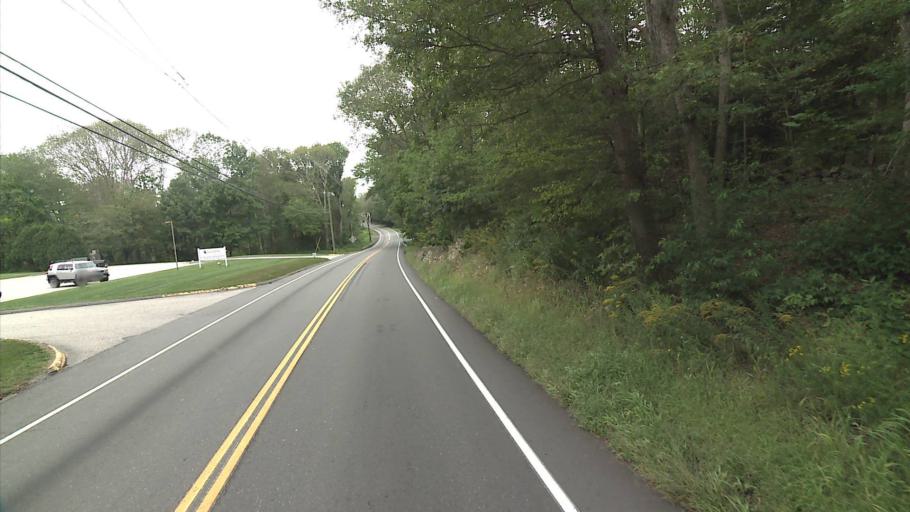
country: US
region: Connecticut
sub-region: New London County
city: Montville Center
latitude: 41.4721
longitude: -72.2596
